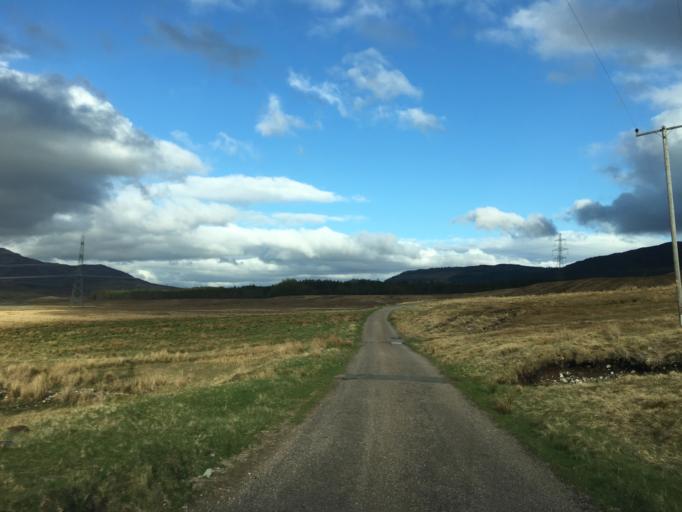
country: GB
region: Scotland
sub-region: Highland
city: Kingussie
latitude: 57.0135
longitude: -4.4209
